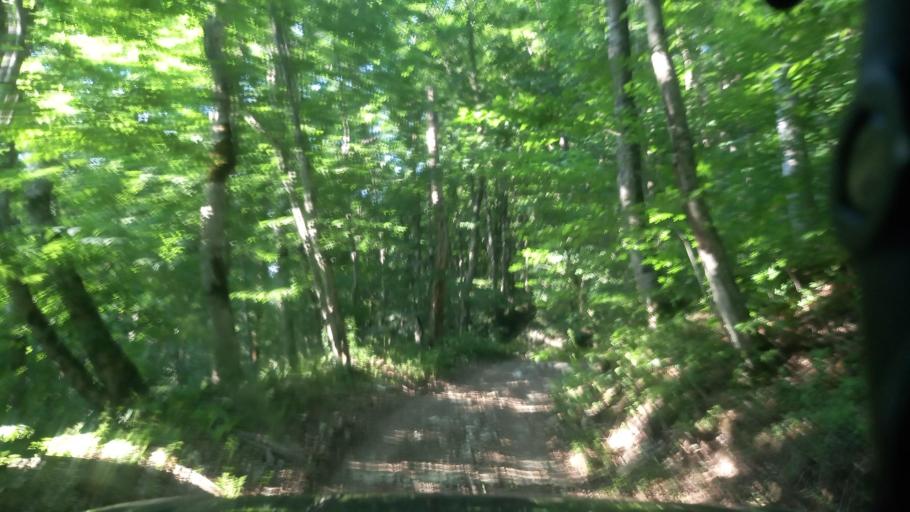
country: RU
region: Krasnodarskiy
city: Pshada
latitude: 44.5951
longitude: 38.2816
